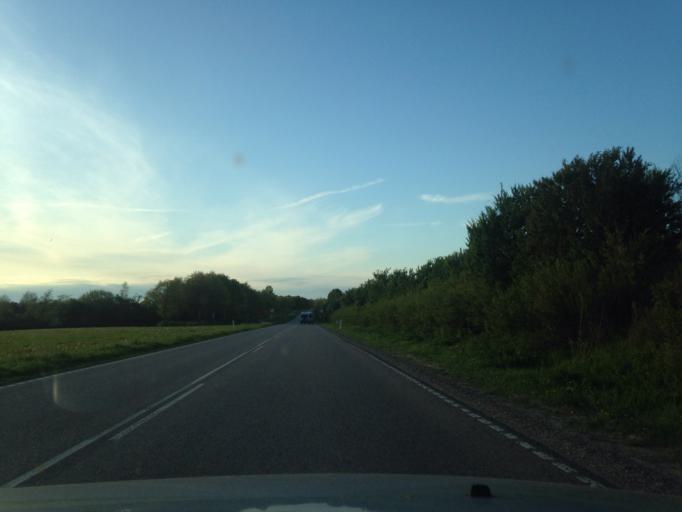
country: DK
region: Capital Region
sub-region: Hoje-Taastrup Kommune
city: Flong
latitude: 55.6377
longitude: 12.1932
